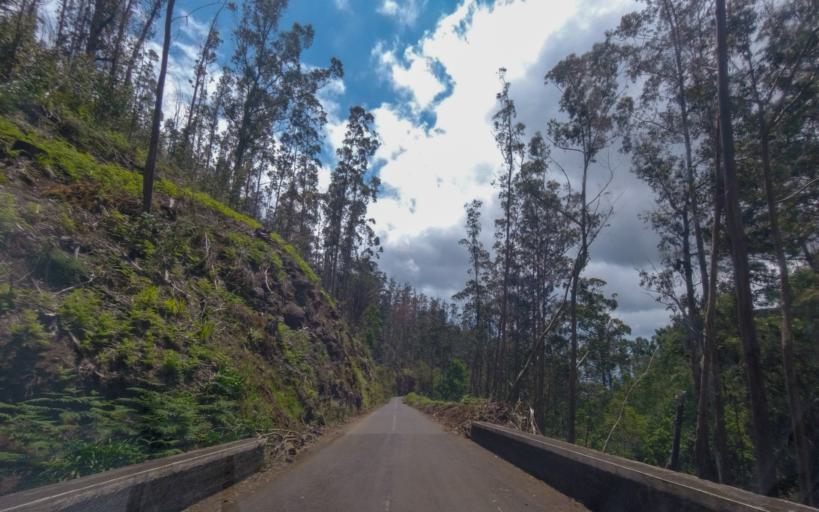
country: PT
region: Madeira
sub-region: Funchal
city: Nossa Senhora do Monte
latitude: 32.6799
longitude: -16.8799
